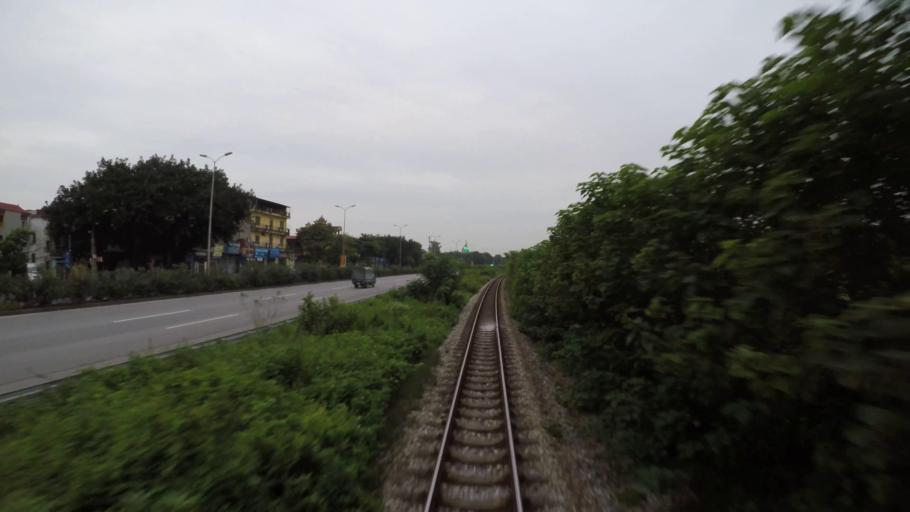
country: VN
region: Ha Noi
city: Trau Quy
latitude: 21.0110
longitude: 105.9521
